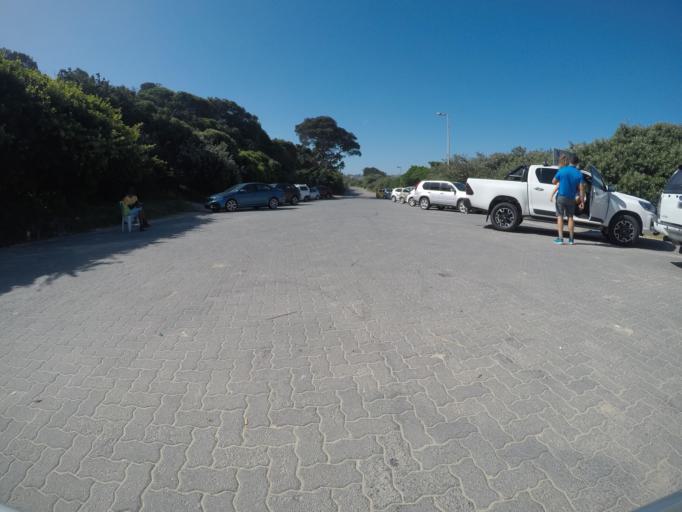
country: ZA
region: Eastern Cape
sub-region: Buffalo City Metropolitan Municipality
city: East London
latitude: -32.9880
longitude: 27.9490
